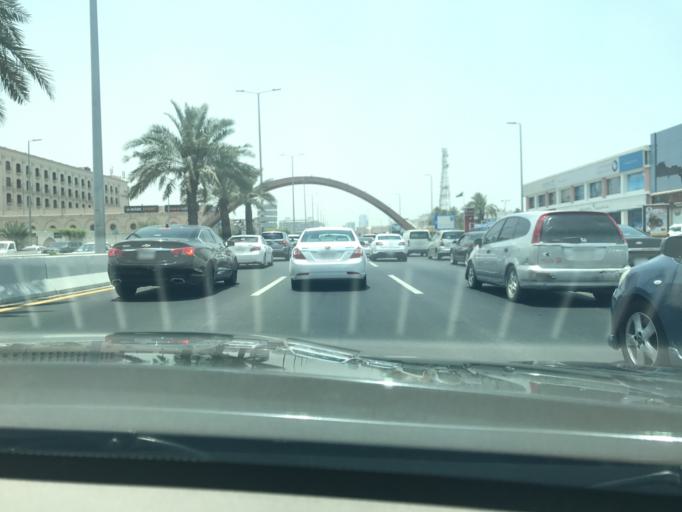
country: SA
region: Makkah
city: Jeddah
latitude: 21.5366
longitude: 39.1777
